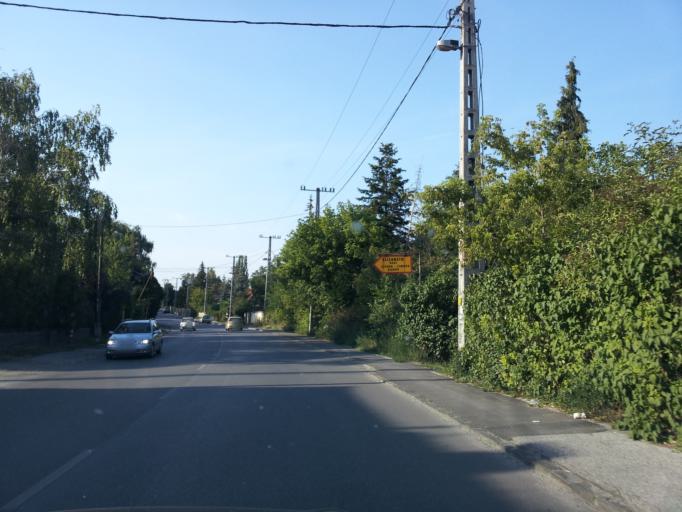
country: HU
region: Pest
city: Leanyfalu
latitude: 47.6994
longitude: 19.0888
